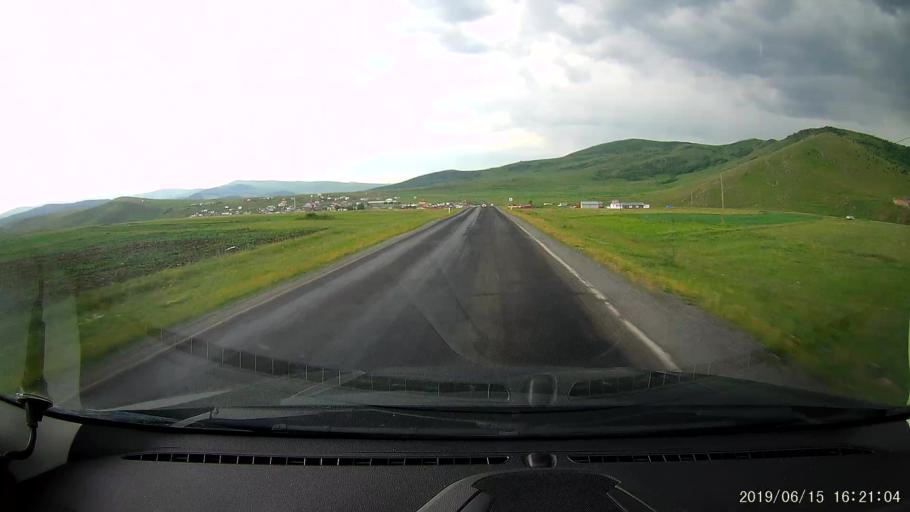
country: TR
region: Ardahan
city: Hanak
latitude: 41.2033
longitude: 42.8463
